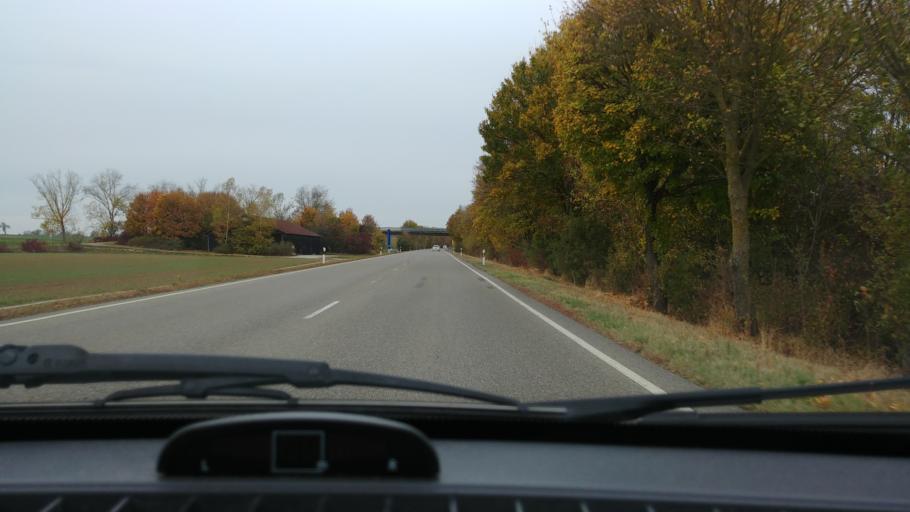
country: DE
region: Baden-Wuerttemberg
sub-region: Regierungsbezirk Stuttgart
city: Wallhausen
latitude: 49.1927
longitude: 10.0700
